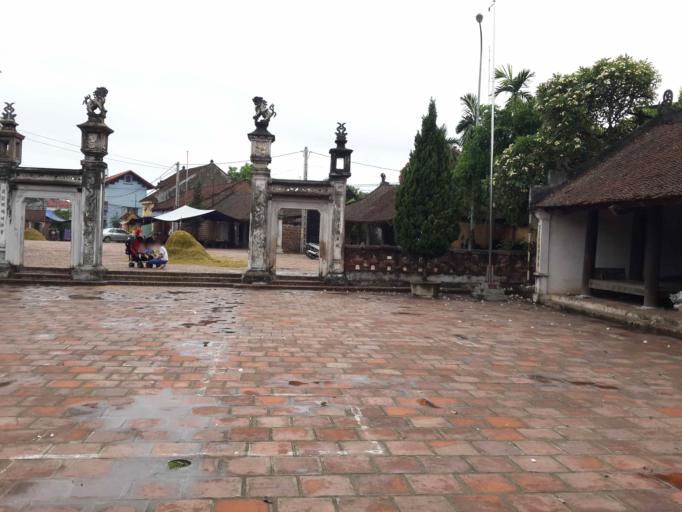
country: VN
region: Ha Noi
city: Son Tay
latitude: 21.1586
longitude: 105.4702
